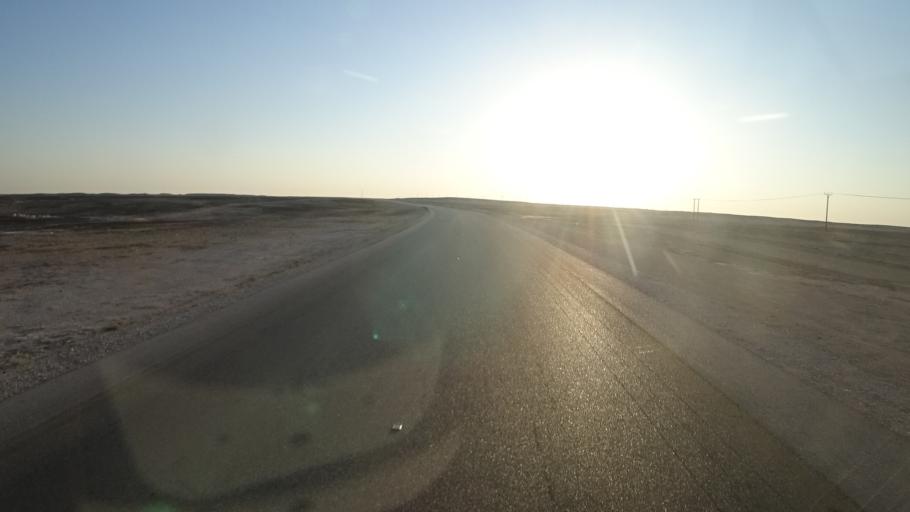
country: OM
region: Zufar
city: Salalah
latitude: 17.5539
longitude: 53.4323
